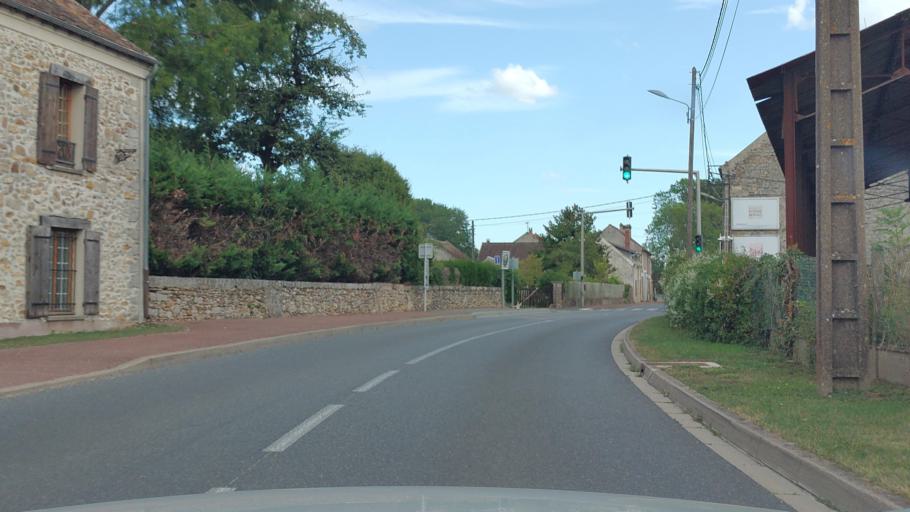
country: FR
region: Ile-de-France
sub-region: Departement de Seine-et-Marne
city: Le Chatelet-en-Brie
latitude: 48.5432
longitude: 2.8084
